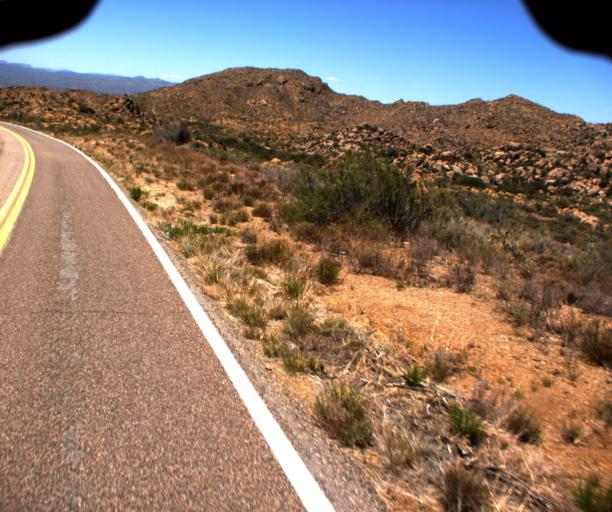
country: US
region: Arizona
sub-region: Yavapai County
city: Bagdad
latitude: 34.4449
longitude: -112.9551
